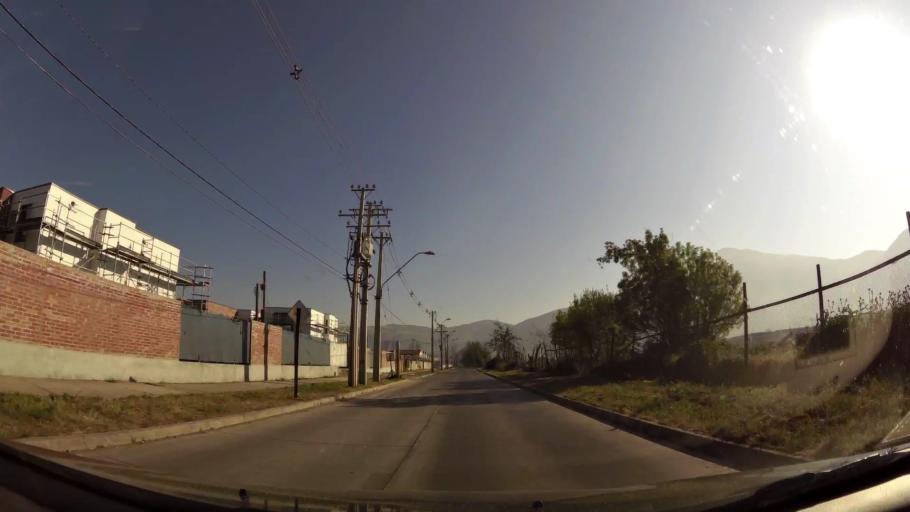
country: CL
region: Santiago Metropolitan
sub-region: Provincia de Chacabuco
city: Chicureo Abajo
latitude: -33.3665
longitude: -70.6650
